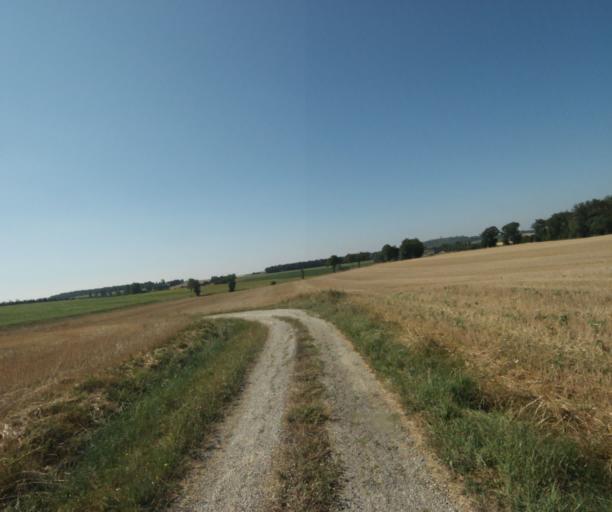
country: FR
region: Midi-Pyrenees
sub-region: Departement de la Haute-Garonne
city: Saint-Felix-Lauragais
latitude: 43.5127
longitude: 1.9180
